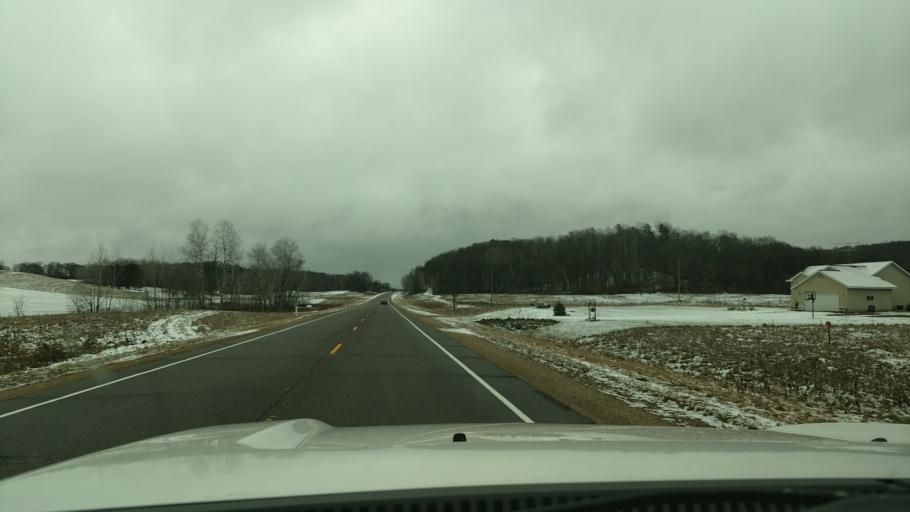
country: US
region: Wisconsin
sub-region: Dunn County
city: Tainter Lake
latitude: 45.1223
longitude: -91.8804
